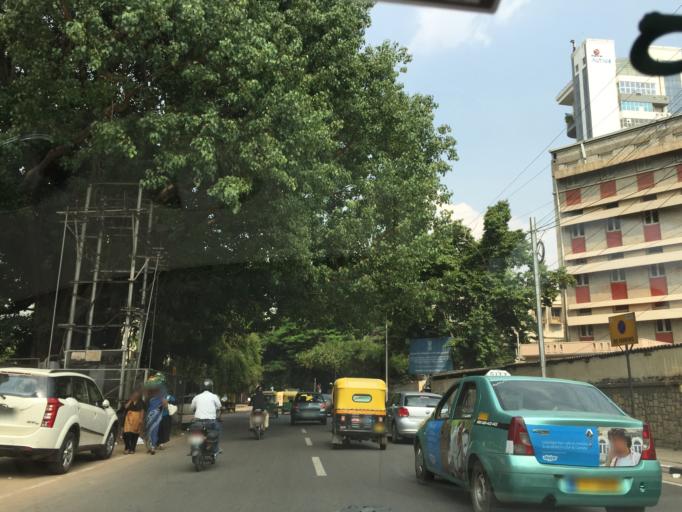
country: IN
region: Karnataka
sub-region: Bangalore Urban
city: Bangalore
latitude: 12.9825
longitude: 77.5977
